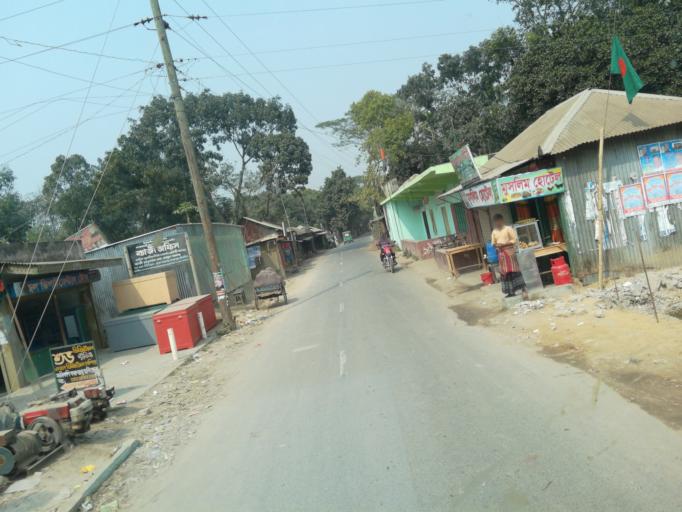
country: BD
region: Dhaka
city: Nagarpur
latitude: 23.9971
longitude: 89.8464
